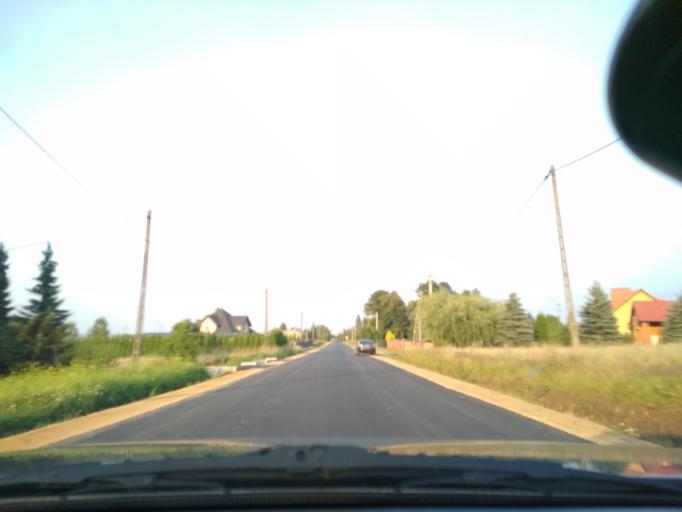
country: PL
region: Lesser Poland Voivodeship
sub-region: Powiat olkuski
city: Wolbrom
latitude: 50.4074
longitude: 19.8182
